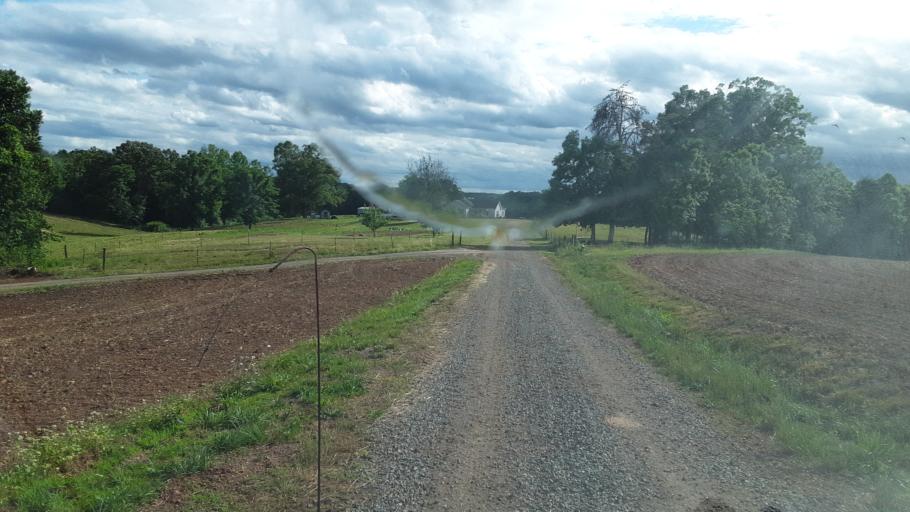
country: US
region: Virginia
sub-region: Pittsylvania County
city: Chatham
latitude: 36.8455
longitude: -79.4028
